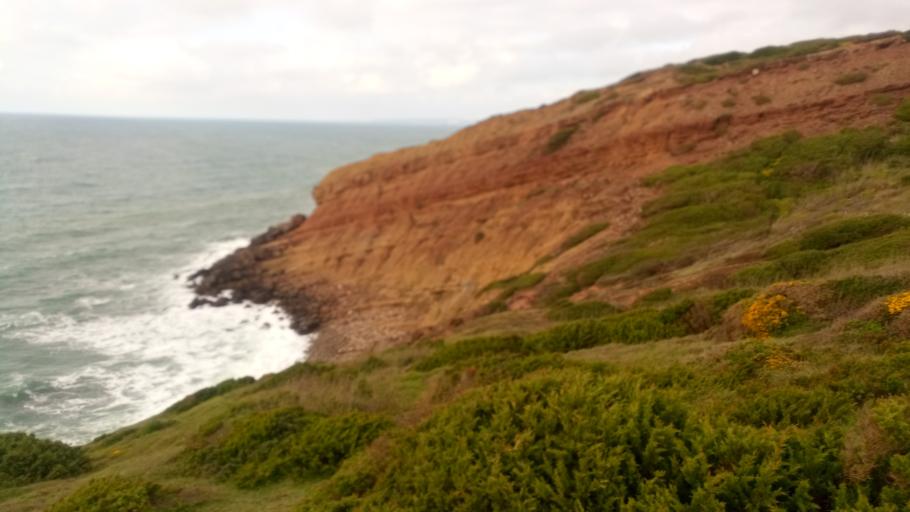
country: PT
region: Leiria
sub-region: Caldas da Rainha
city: Caldas da Rainha
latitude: 39.4912
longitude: -9.1796
